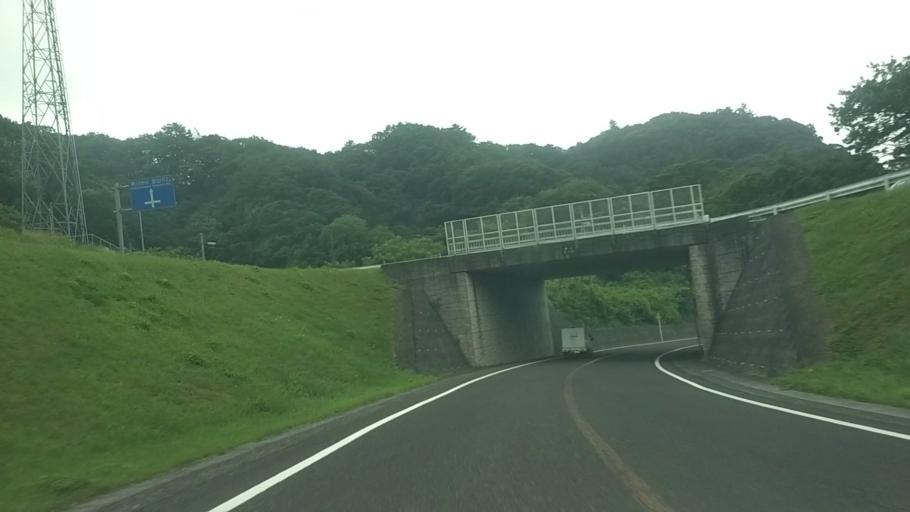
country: JP
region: Chiba
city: Kawaguchi
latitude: 35.1575
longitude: 140.0679
